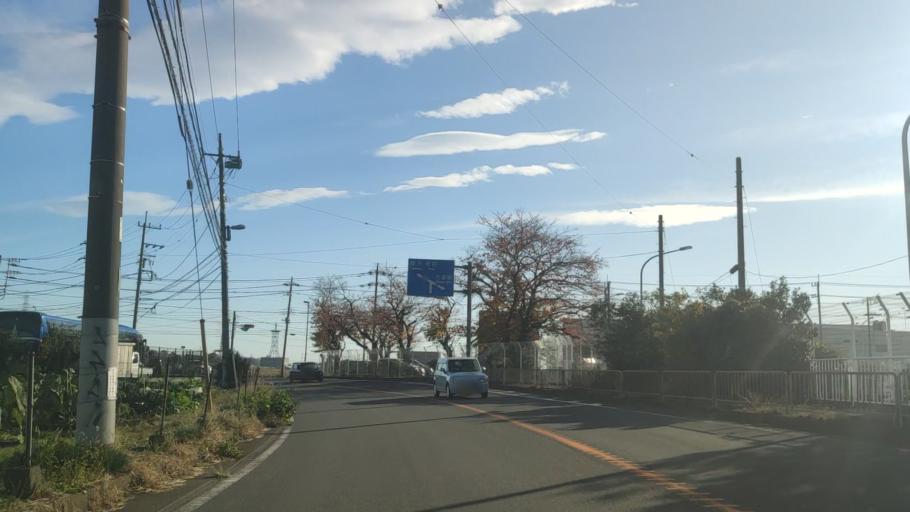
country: JP
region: Kanagawa
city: Atsugi
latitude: 35.4223
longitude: 139.3877
